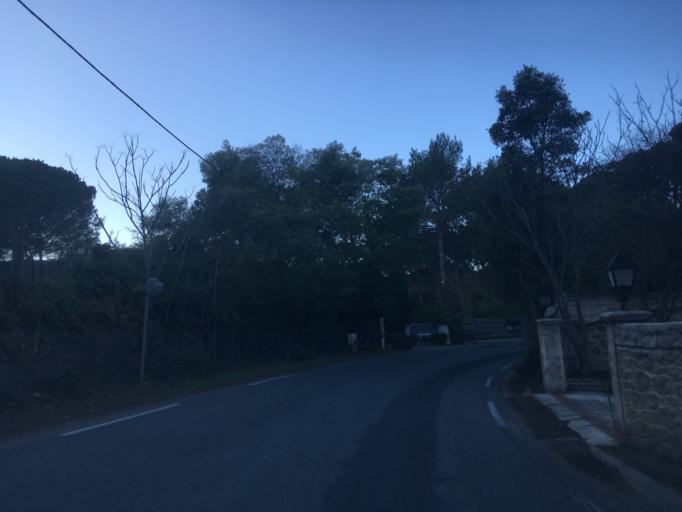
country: FR
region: Provence-Alpes-Cote d'Azur
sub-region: Departement du Var
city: Le Plan-de-la-Tour
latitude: 43.3292
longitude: 6.5452
